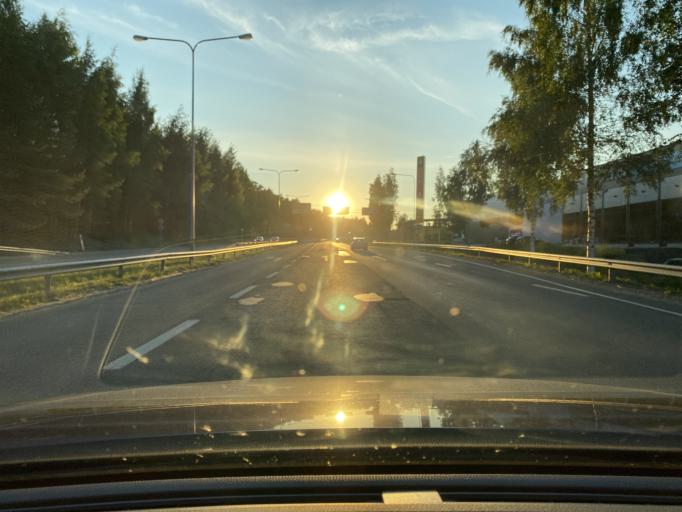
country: FI
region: Pirkanmaa
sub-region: Tampere
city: Yloejaervi
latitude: 61.5304
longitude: 23.6359
